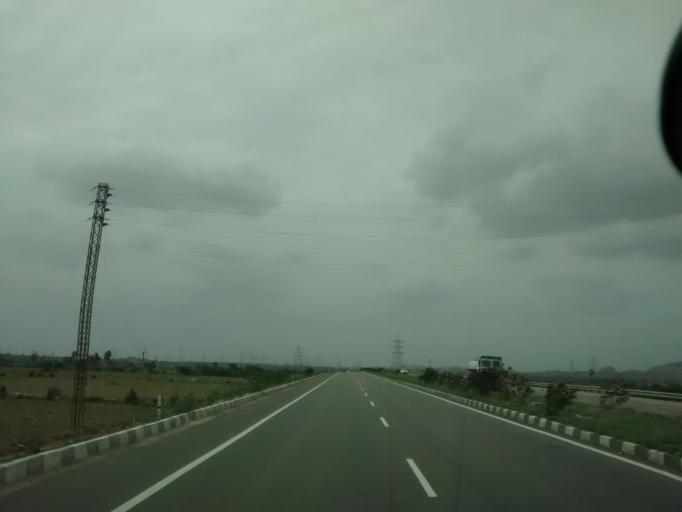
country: IN
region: Andhra Pradesh
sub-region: Kurnool
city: Ramapuram
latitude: 15.1215
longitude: 77.6606
